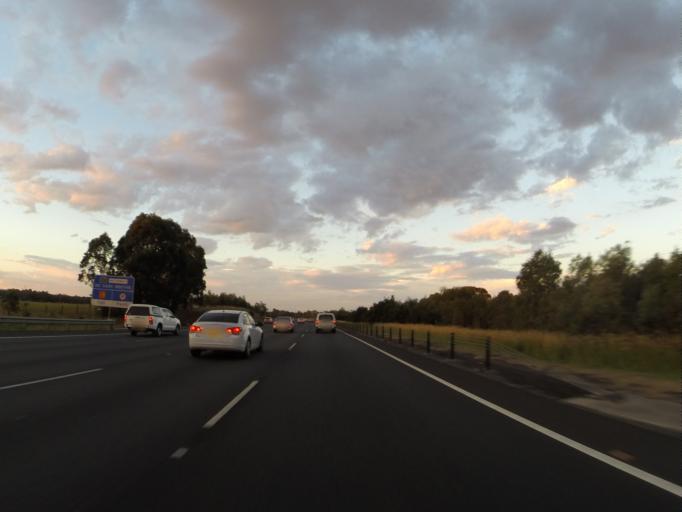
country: AU
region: New South Wales
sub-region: Campbelltown Municipality
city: Ingleburn
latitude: -33.9751
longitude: 150.8715
